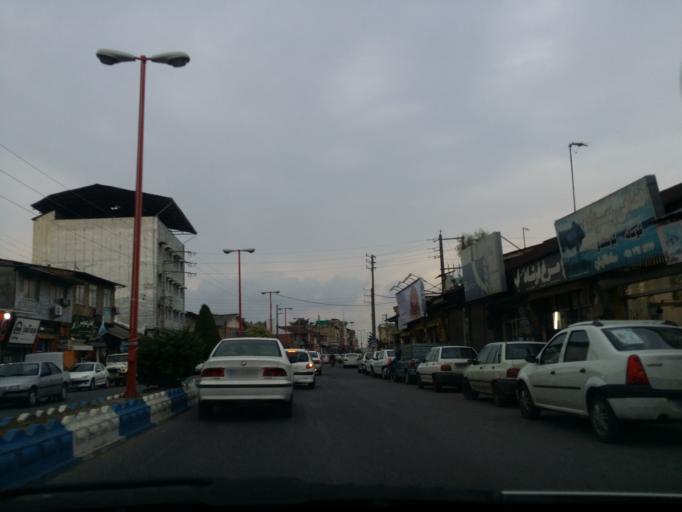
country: IR
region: Mazandaran
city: `Abbasabad
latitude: 36.7265
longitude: 51.1048
